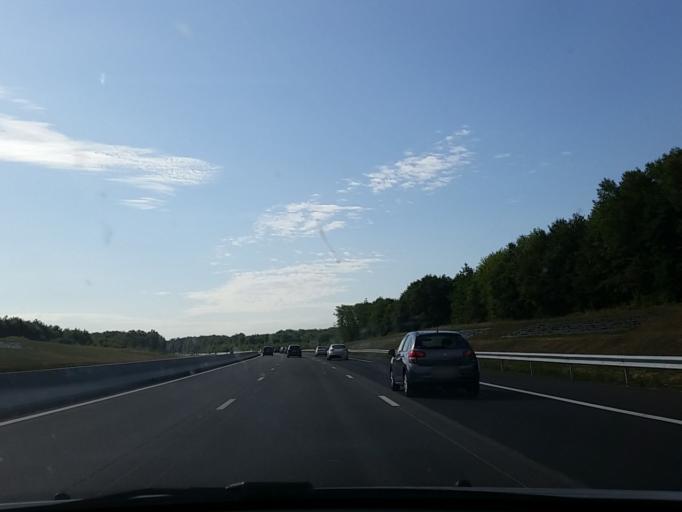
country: FR
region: Centre
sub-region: Departement du Loir-et-Cher
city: Theillay
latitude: 47.2594
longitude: 2.0455
